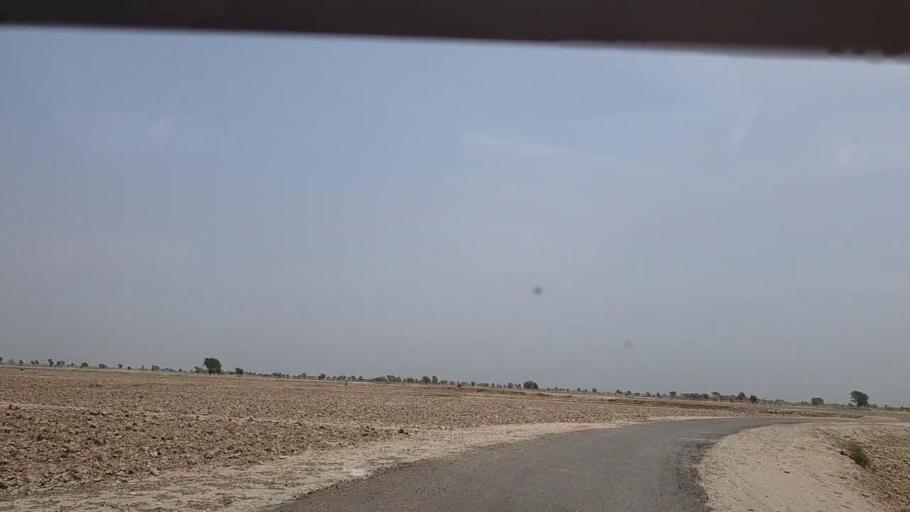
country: PK
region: Sindh
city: Khairpur Nathan Shah
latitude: 27.0144
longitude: 67.6242
